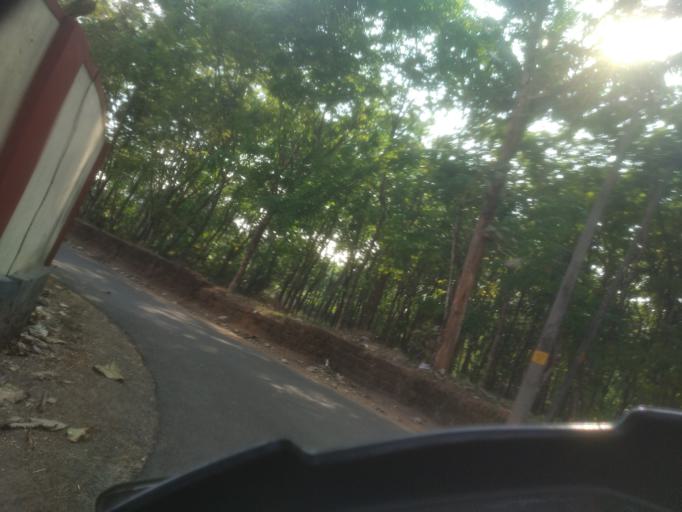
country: IN
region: Kerala
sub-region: Ernakulam
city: Piravam
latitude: 9.8781
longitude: 76.5519
